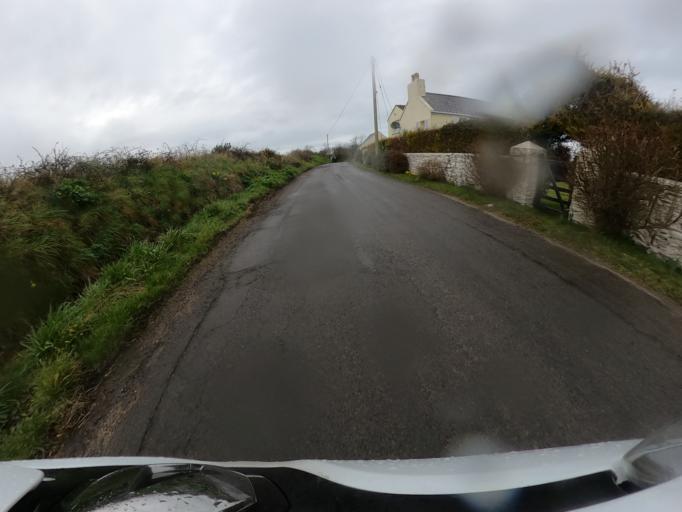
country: IM
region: Ramsey
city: Ramsey
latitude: 54.3735
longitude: -4.4506
